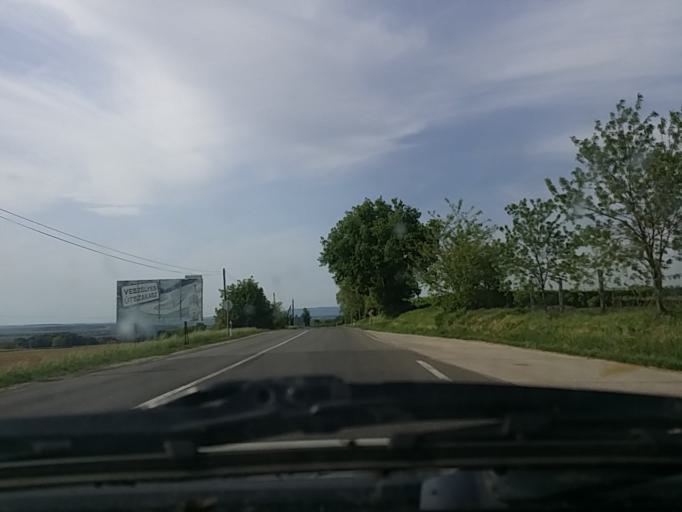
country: HU
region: Baranya
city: Harkany
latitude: 45.8905
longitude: 18.2346
